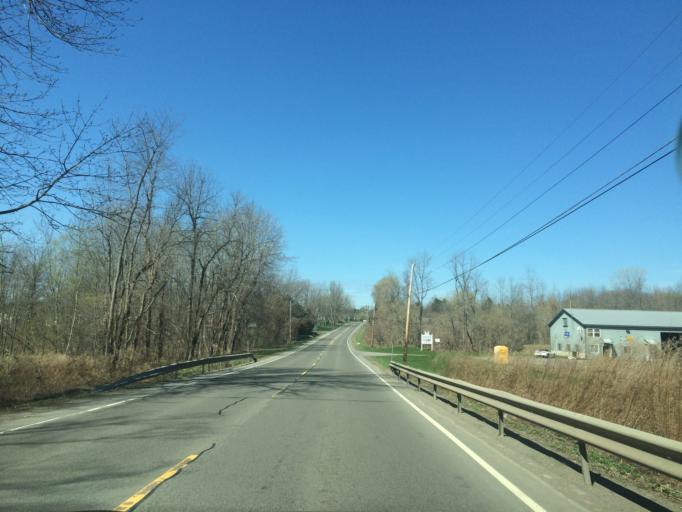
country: US
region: New York
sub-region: Wayne County
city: Macedon
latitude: 43.0943
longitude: -77.3448
